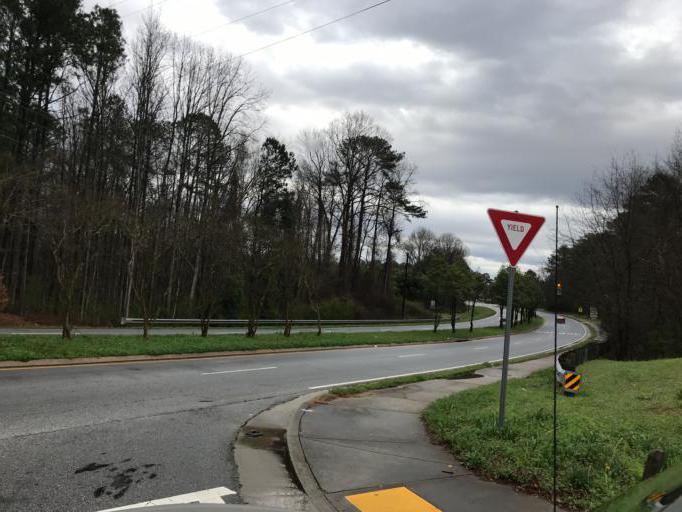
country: US
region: Georgia
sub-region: DeKalb County
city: Panthersville
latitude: 33.6796
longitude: -84.2236
